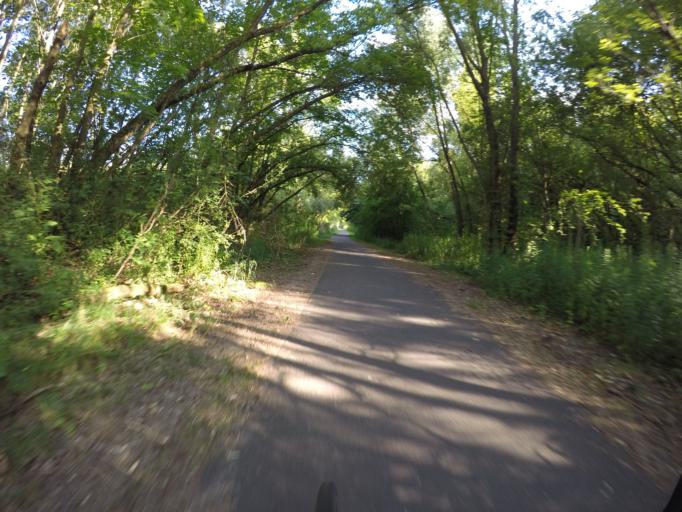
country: DE
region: Berlin
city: Stadtrandsiedlung Malchow
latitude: 52.5771
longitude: 13.4919
